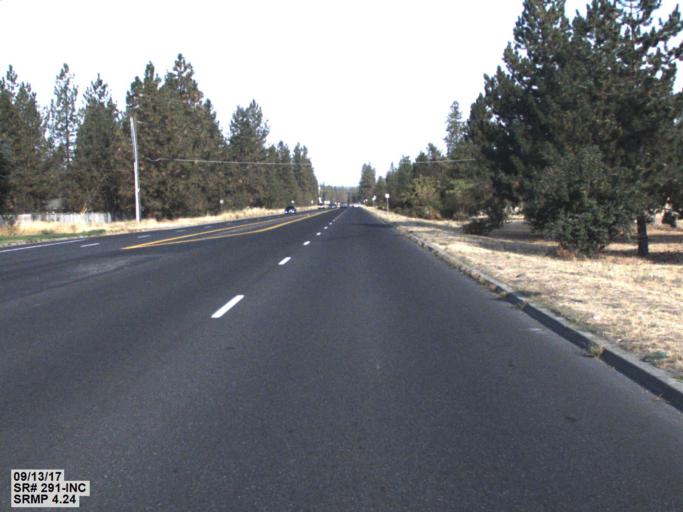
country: US
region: Washington
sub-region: Spokane County
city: Town and Country
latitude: 47.7260
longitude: -117.4956
